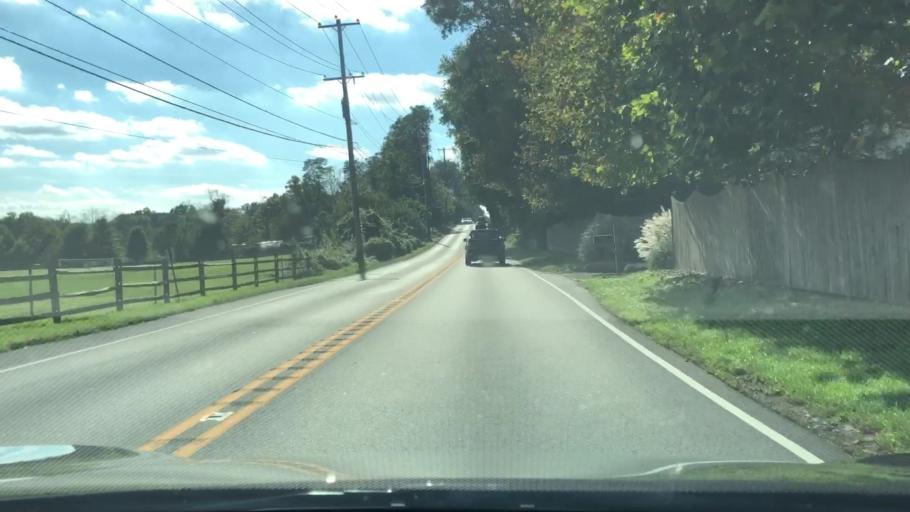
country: US
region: Pennsylvania
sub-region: Chester County
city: West Chester
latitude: 39.9355
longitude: -75.5424
